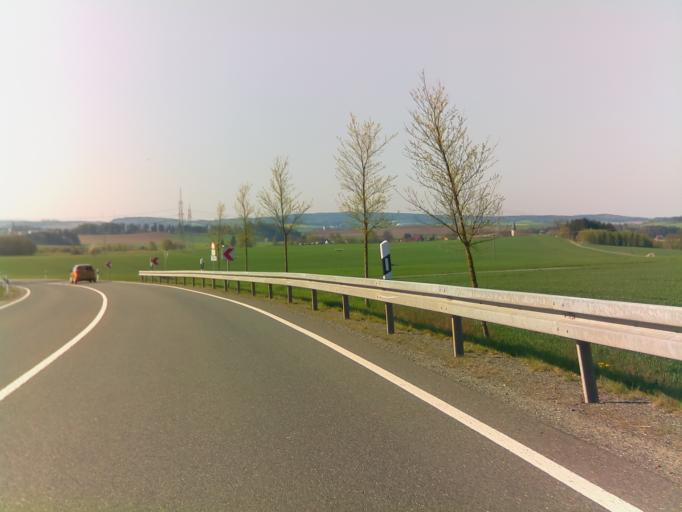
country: DE
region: Thuringia
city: Pormitz
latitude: 50.6278
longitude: 11.8140
